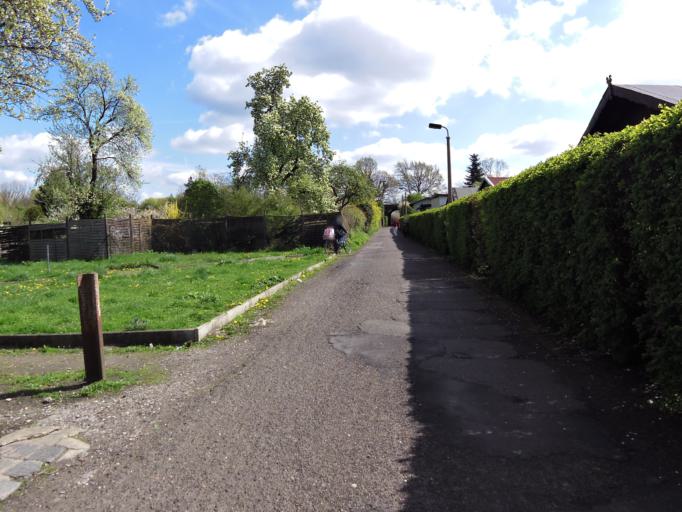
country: DE
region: Saxony
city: Leipzig
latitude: 51.3403
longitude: 12.4195
